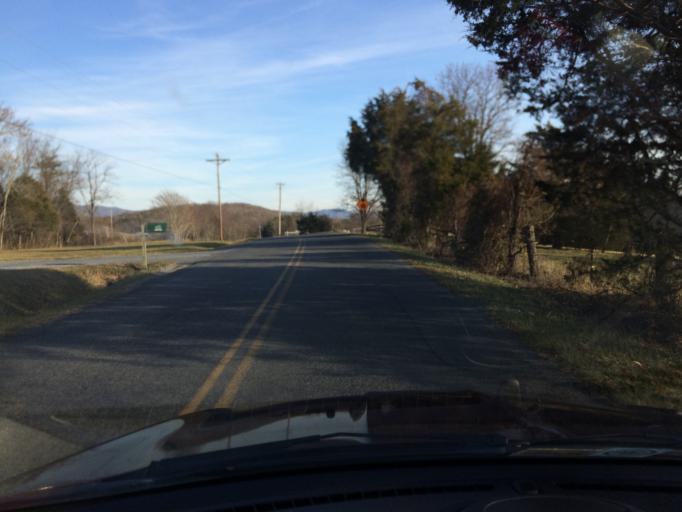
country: US
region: Virginia
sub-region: Botetourt County
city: Fincastle
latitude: 37.6196
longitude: -79.8283
